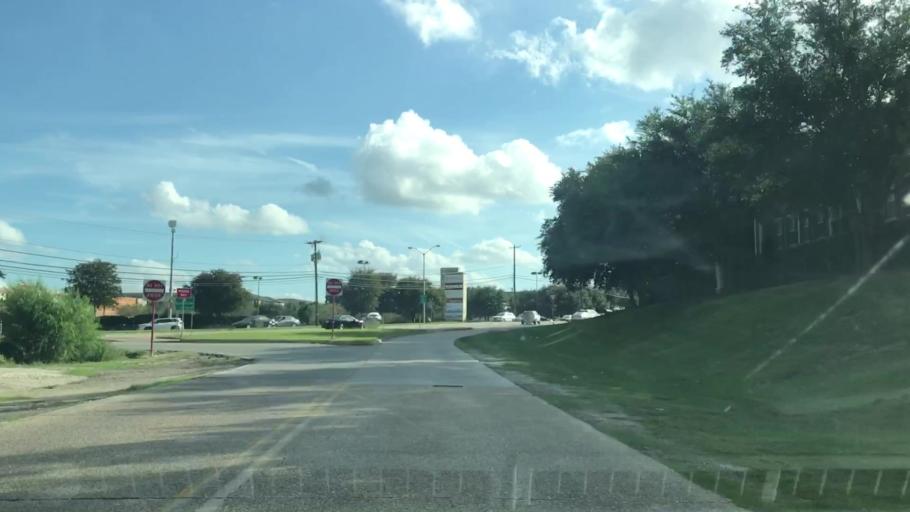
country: US
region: Texas
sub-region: Dallas County
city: Highland Park
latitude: 32.8589
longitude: -96.7552
